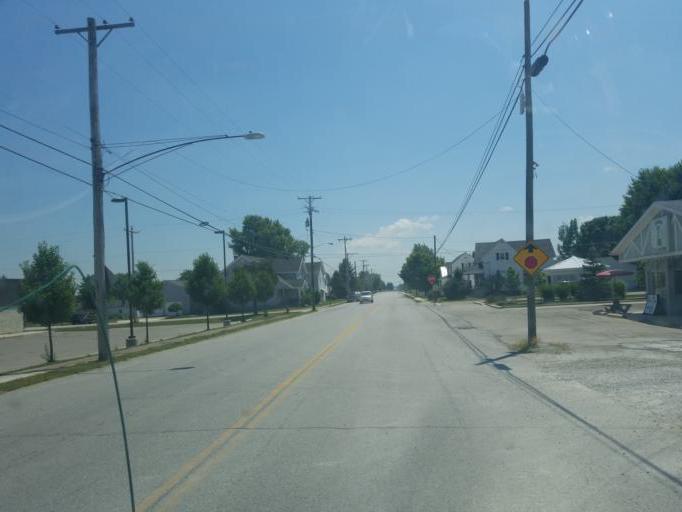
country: US
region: Ohio
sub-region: Shelby County
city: Botkins
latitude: 40.4672
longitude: -84.1821
